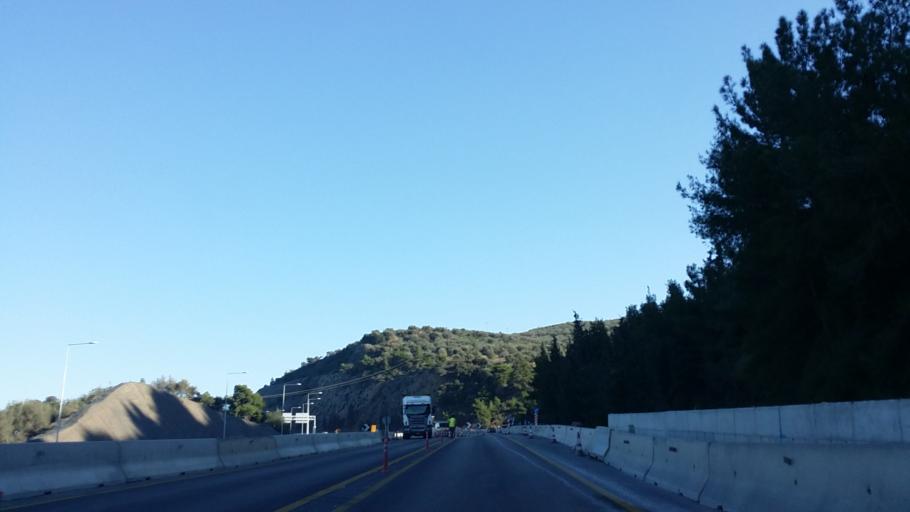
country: GR
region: West Greece
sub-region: Nomos Achaias
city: Akrata
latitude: 38.1749
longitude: 22.2429
